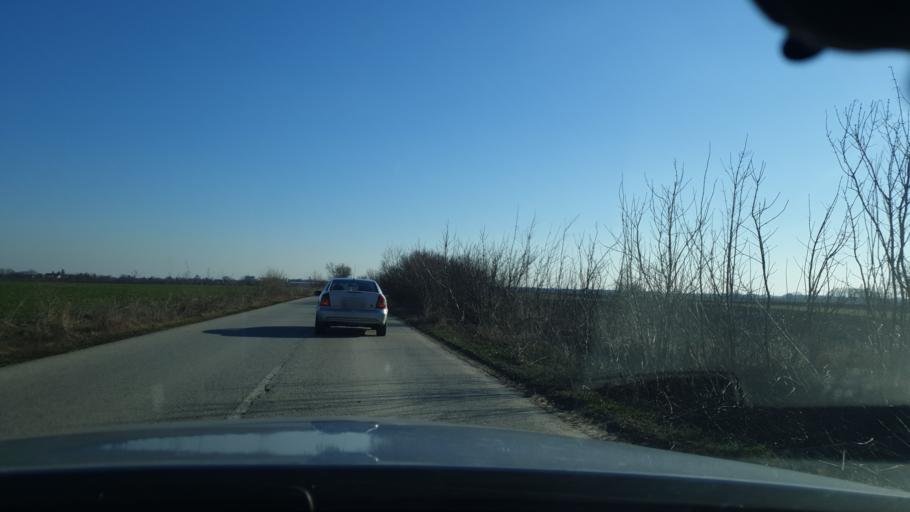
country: RS
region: Autonomna Pokrajina Vojvodina
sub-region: Sremski Okrug
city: Ruma
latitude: 45.0336
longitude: 19.8092
